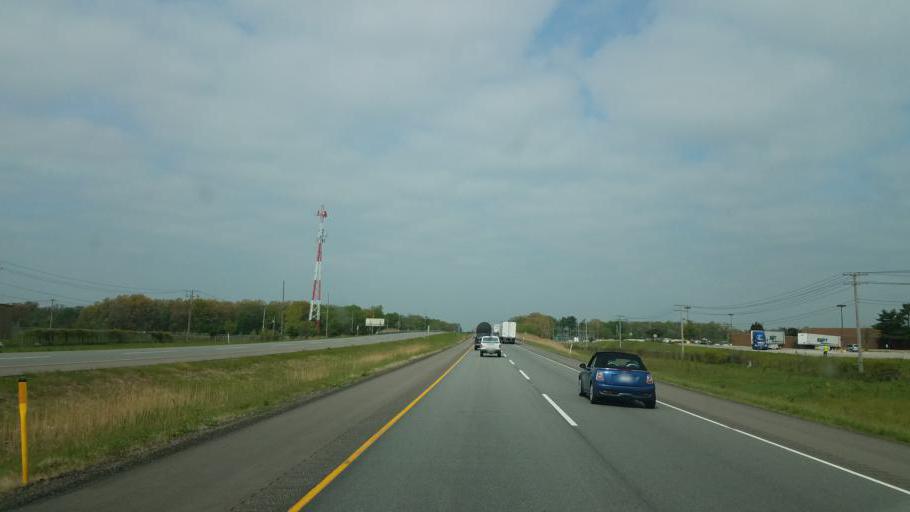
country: US
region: Indiana
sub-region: Saint Joseph County
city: Georgetown
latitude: 41.7163
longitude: -86.1895
